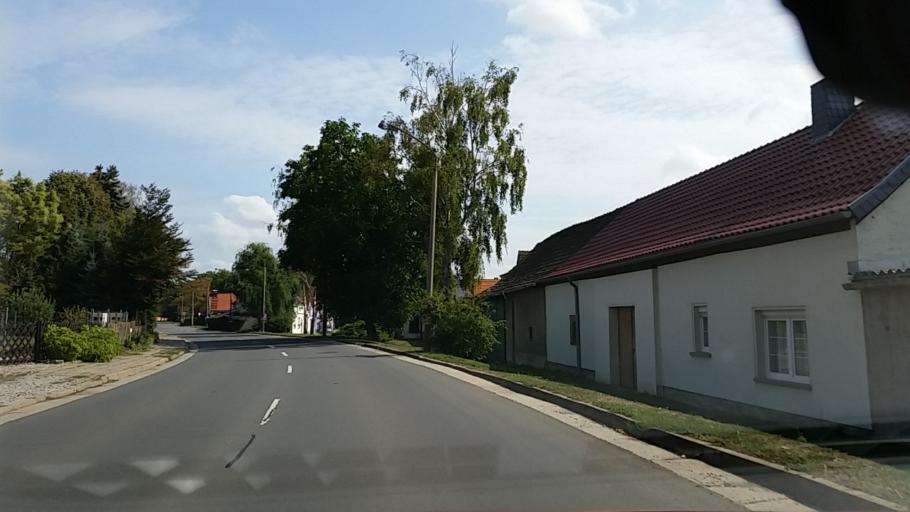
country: DE
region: Thuringia
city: Ringleben
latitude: 51.3675
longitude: 11.2233
